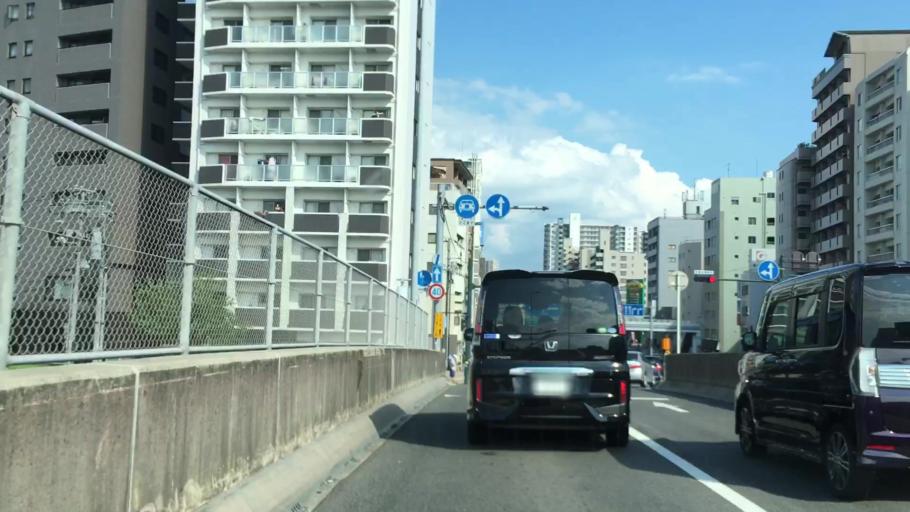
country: JP
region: Hiroshima
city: Hiroshima-shi
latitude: 34.3872
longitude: 132.4406
